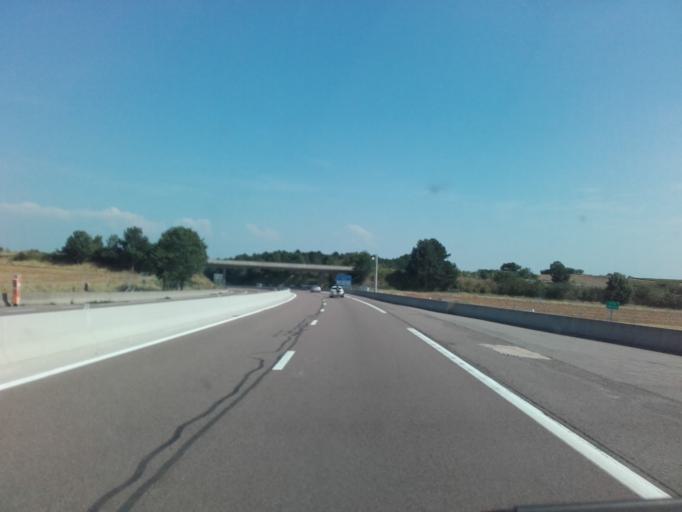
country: FR
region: Bourgogne
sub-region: Departement de la Cote-d'Or
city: Savigny-les-Beaune
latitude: 47.0599
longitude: 4.7758
